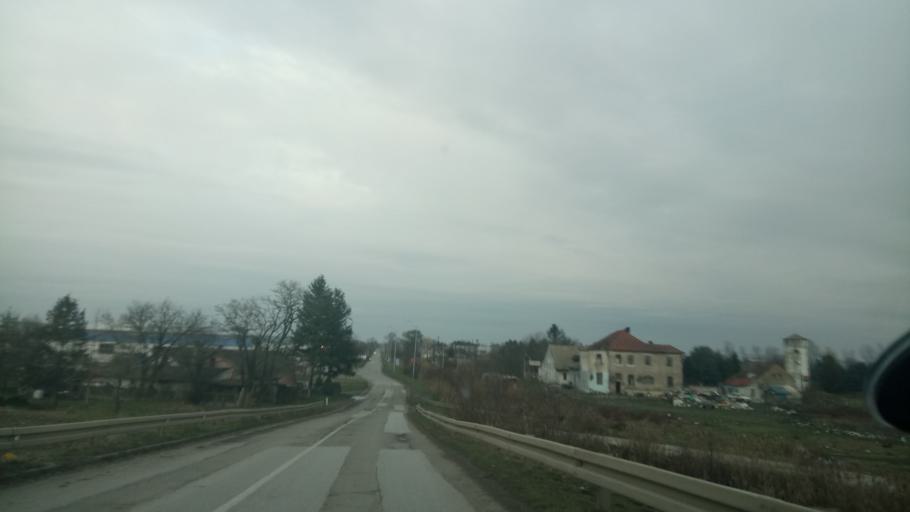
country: RS
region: Autonomna Pokrajina Vojvodina
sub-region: Sremski Okrug
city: Stara Pazova
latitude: 44.9667
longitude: 20.1616
